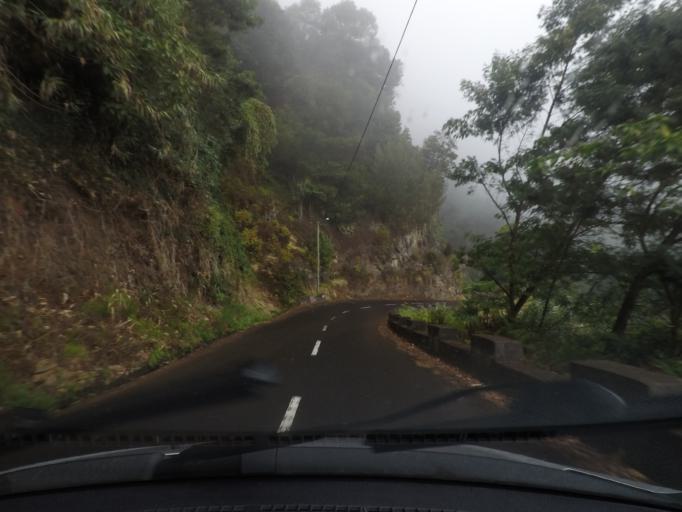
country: PT
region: Madeira
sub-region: Santana
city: Santana
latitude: 32.7742
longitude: -16.8732
